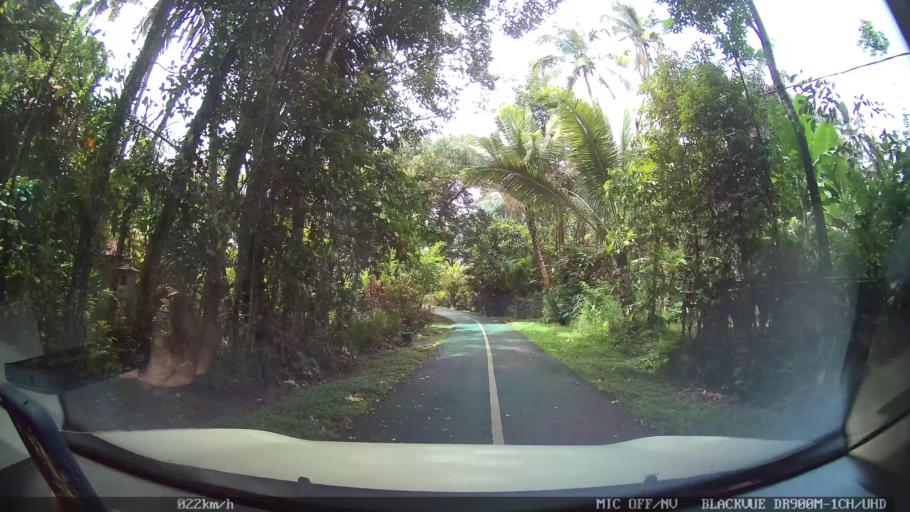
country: ID
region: Bali
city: Bunutan
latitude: -8.4688
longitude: 115.2348
